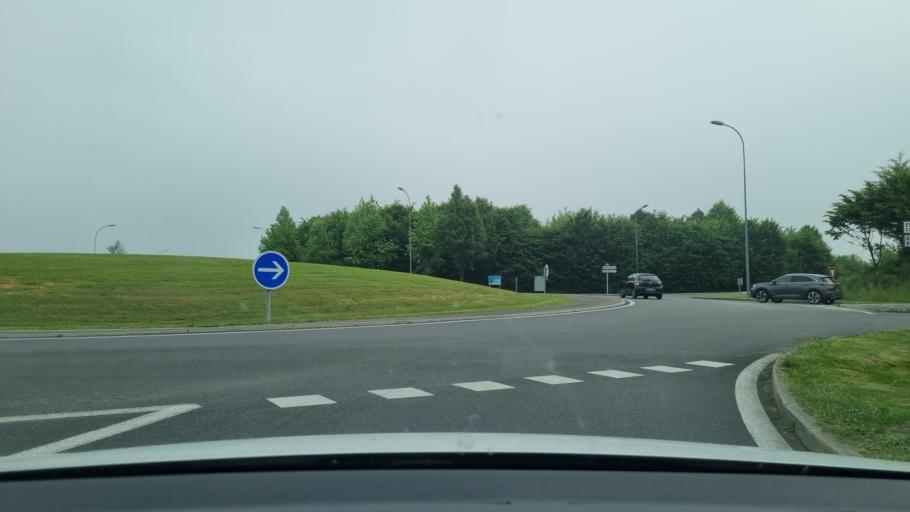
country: FR
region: Aquitaine
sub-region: Departement des Landes
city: Saint-Sever
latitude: 43.7467
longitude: -0.5621
